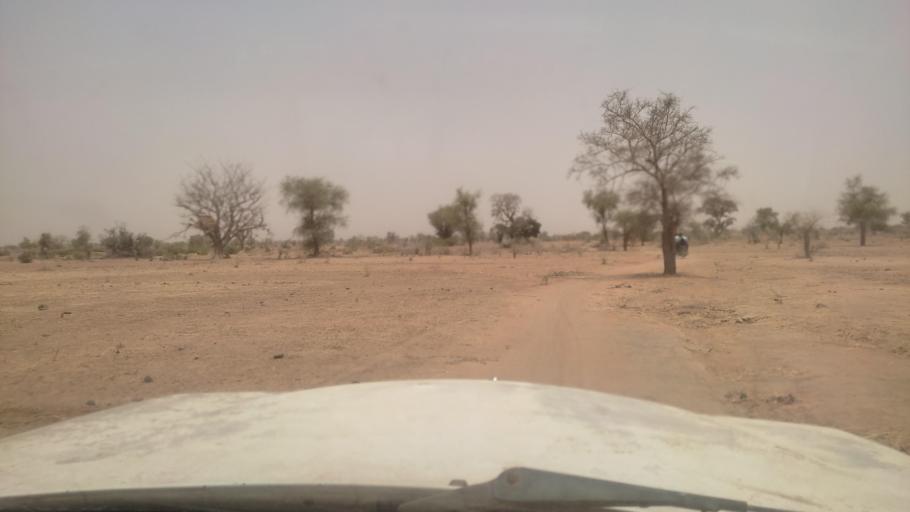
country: BF
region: Est
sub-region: Gnagna Province
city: Bogande
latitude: 13.0345
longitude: -0.0738
